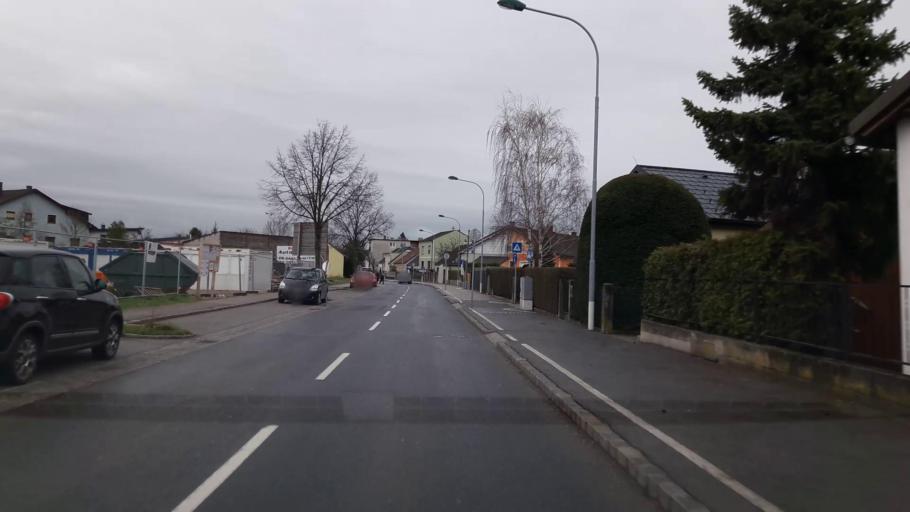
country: AT
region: Burgenland
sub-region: Politischer Bezirk Neusiedl am See
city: Bruckneudorf
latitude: 48.0357
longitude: 16.7828
